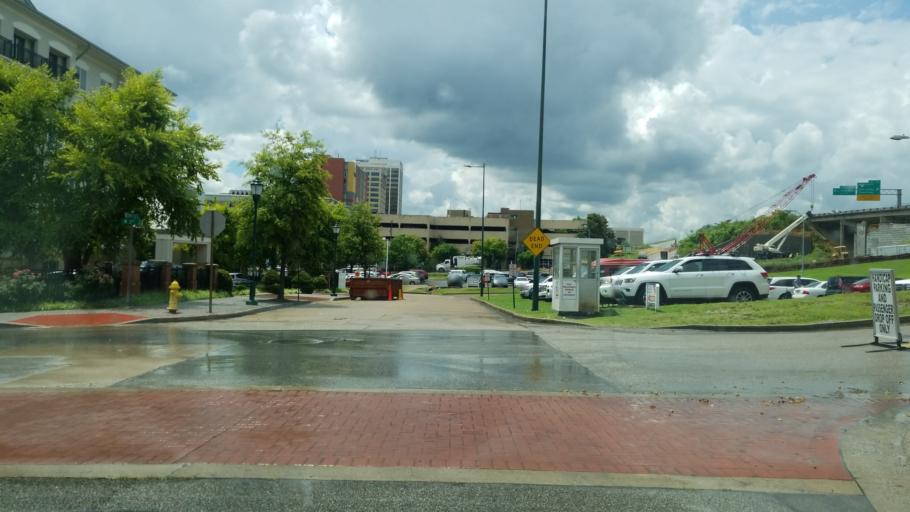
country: US
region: Tennessee
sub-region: Hamilton County
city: Chattanooga
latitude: 35.0536
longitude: -85.3128
